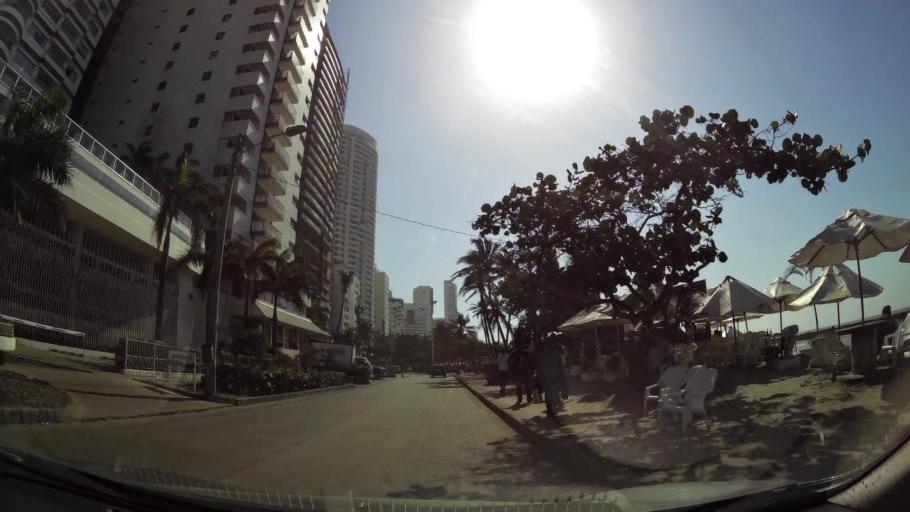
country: CO
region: Bolivar
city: Cartagena
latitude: 10.4047
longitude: -75.5554
